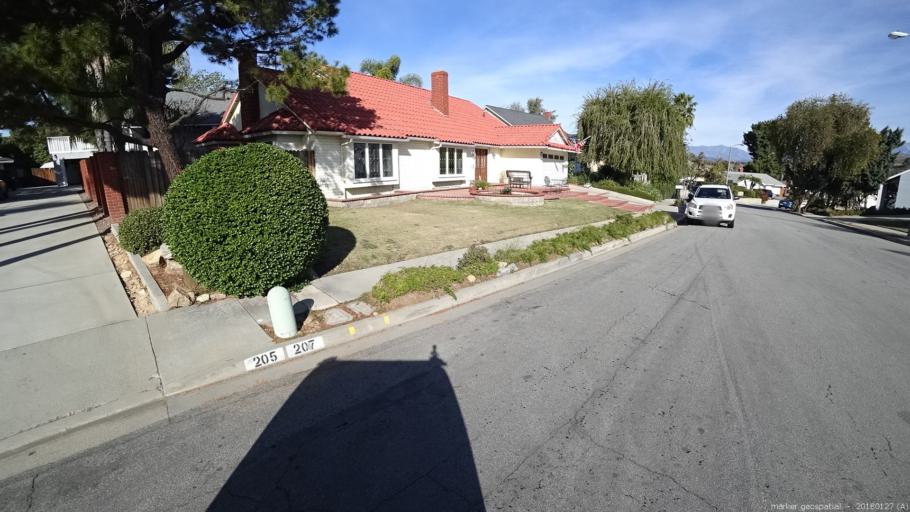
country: US
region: California
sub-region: Los Angeles County
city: Diamond Bar
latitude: 34.0292
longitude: -117.7979
